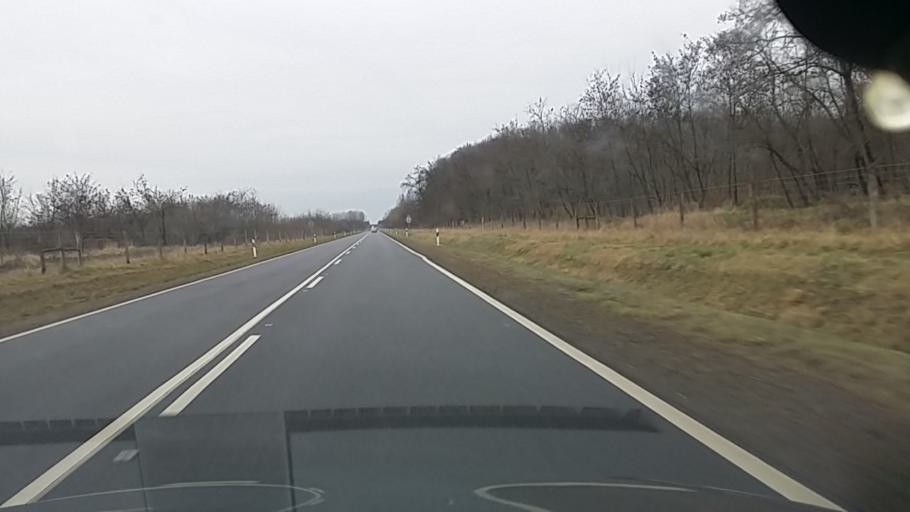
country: HU
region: Hajdu-Bihar
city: Debrecen
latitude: 47.6001
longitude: 21.6193
